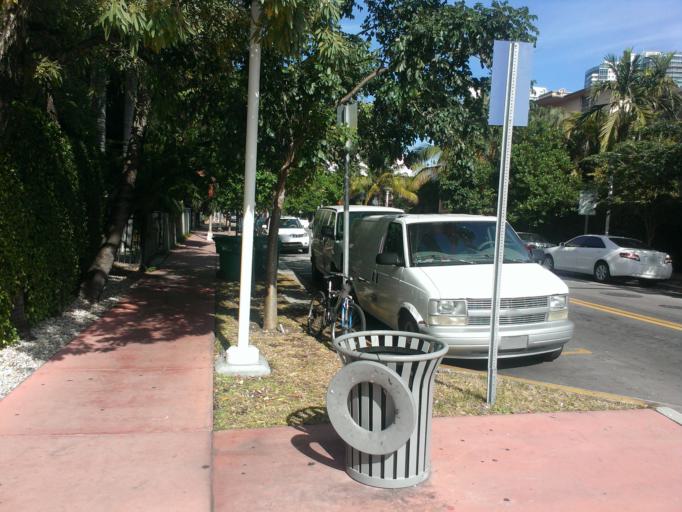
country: US
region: Florida
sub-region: Miami-Dade County
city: Miami Beach
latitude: 25.7924
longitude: -80.1308
